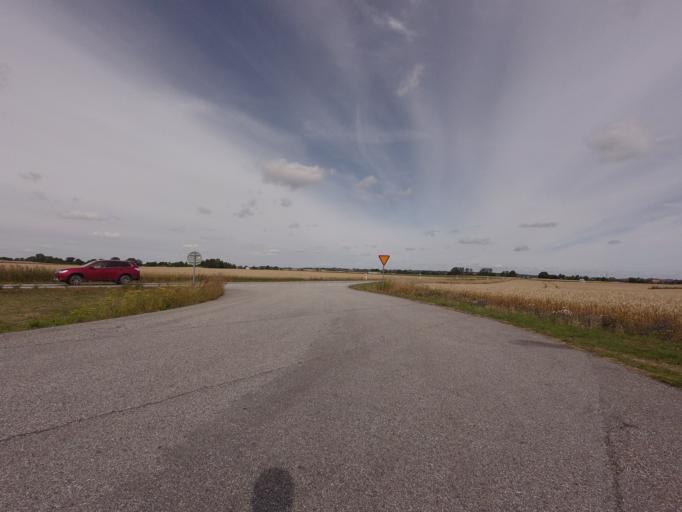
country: SE
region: Skane
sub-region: Simrishamns Kommun
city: Simrishamn
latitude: 55.5354
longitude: 14.3402
